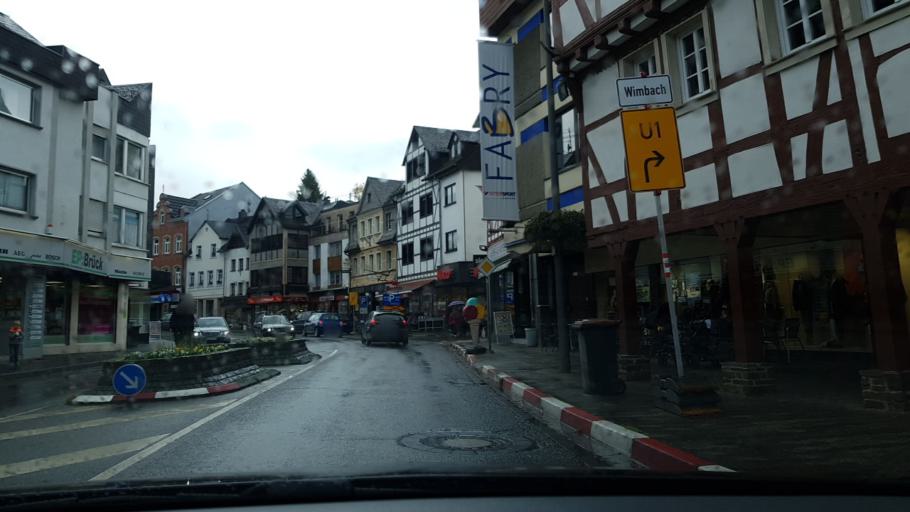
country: DE
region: Rheinland-Pfalz
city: Adenau
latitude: 50.3824
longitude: 6.9298
